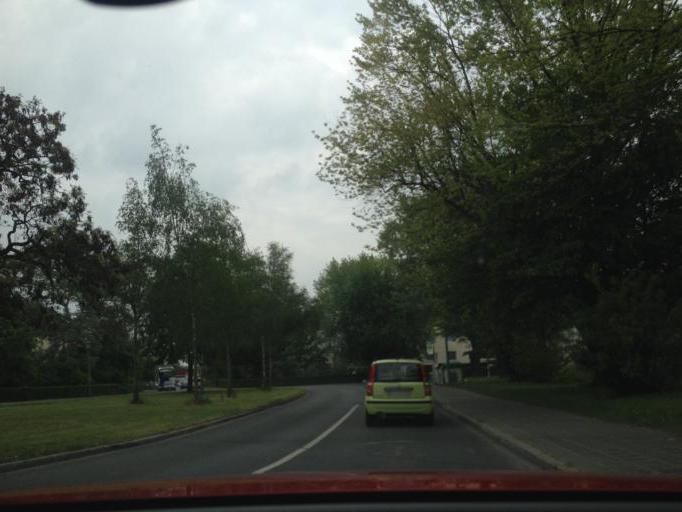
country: DE
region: Bavaria
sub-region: Regierungsbezirk Mittelfranken
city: Furth
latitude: 49.4576
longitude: 10.9968
